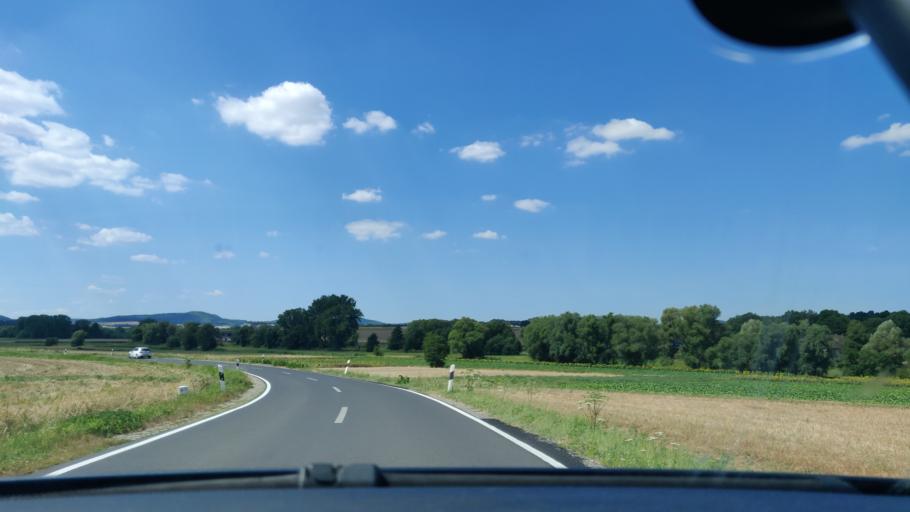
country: DE
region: Hesse
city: Gudensberg
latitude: 51.1559
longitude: 9.3415
